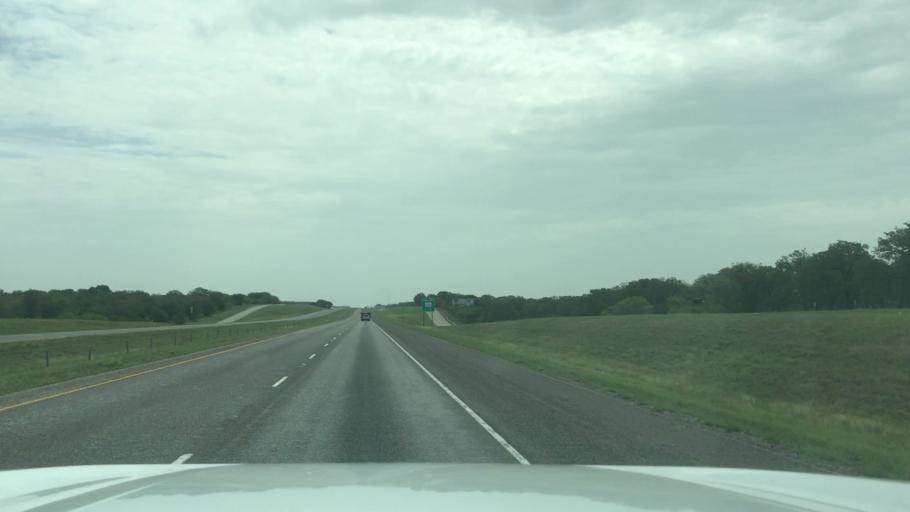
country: US
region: Texas
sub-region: Eastland County
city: Cisco
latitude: 32.3754
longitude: -98.9129
